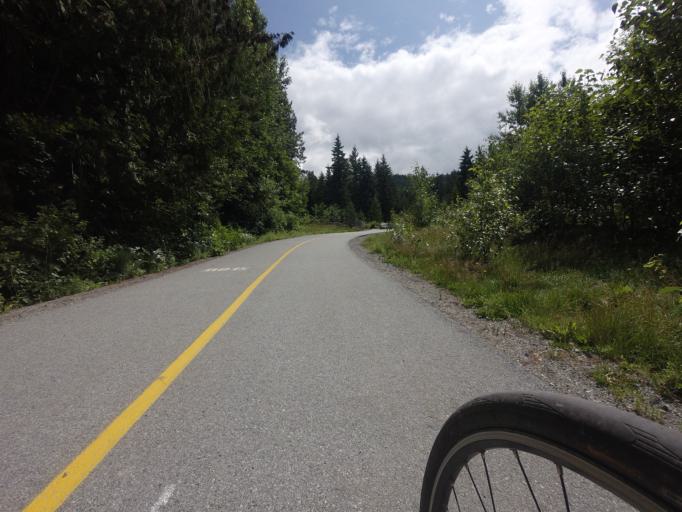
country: CA
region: British Columbia
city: Whistler
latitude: 50.1074
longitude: -122.9791
